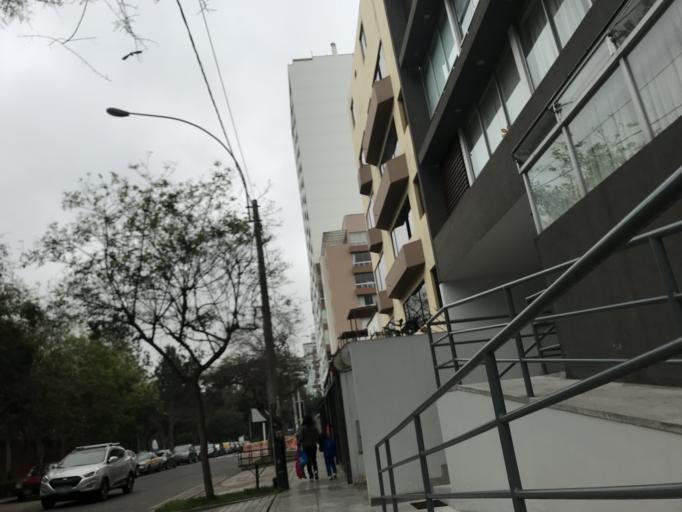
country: PE
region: Lima
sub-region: Lima
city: San Isidro
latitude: -12.0877
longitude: -77.0413
